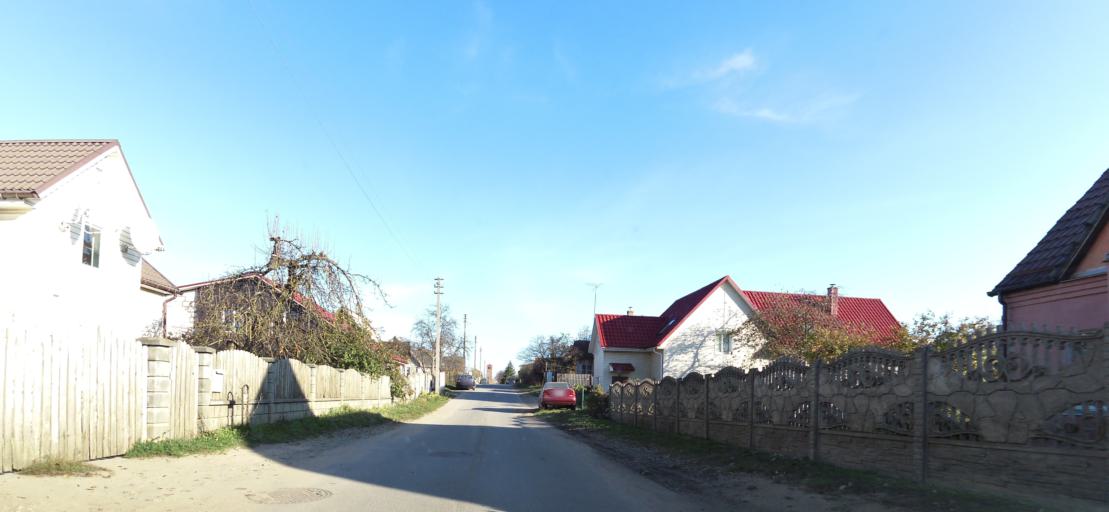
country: LT
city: Lentvaris
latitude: 54.6418
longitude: 25.0390
